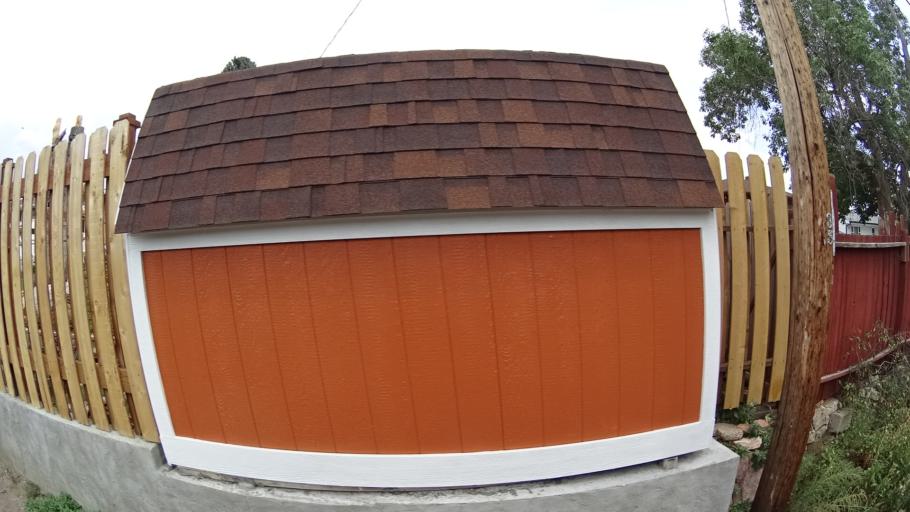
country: US
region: Colorado
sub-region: El Paso County
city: Colorado Springs
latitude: 38.8646
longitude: -104.7821
